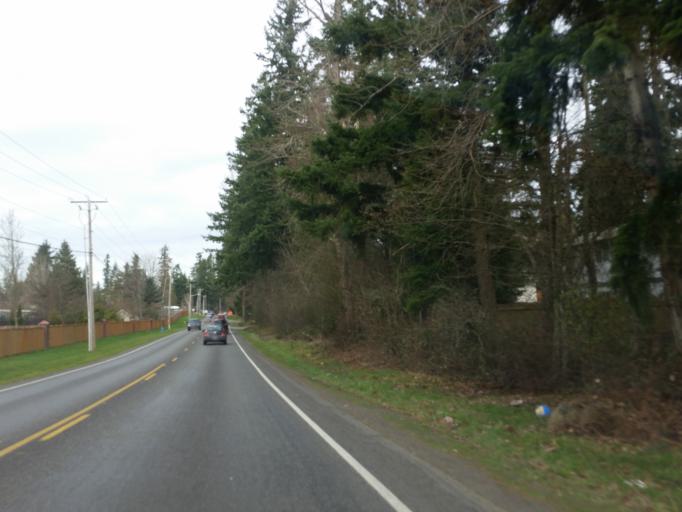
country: US
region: Washington
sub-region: Pierce County
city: South Hill
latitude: 47.1488
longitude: -122.2585
